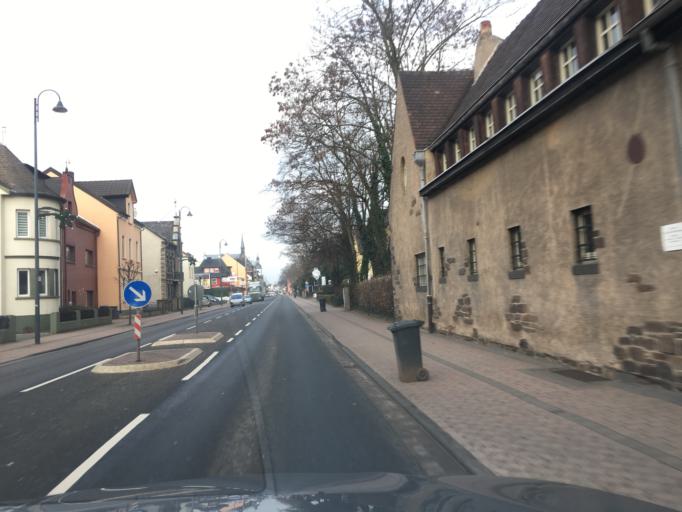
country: DE
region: Rheinland-Pfalz
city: Bad Honningen
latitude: 50.5053
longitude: 7.3038
